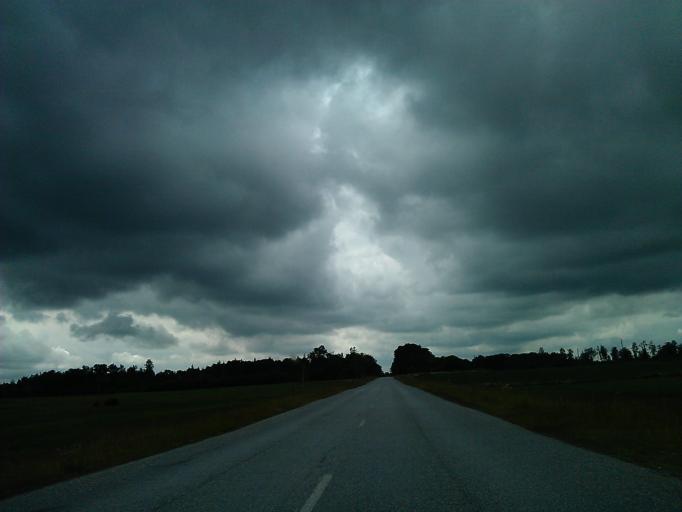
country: LV
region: Aizpute
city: Aizpute
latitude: 56.8199
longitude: 21.7298
